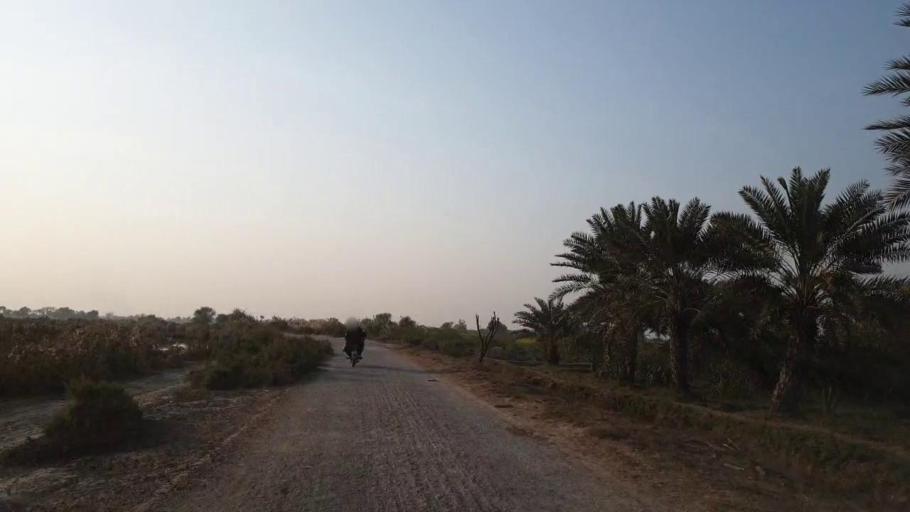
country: PK
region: Sindh
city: Pithoro
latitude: 25.6536
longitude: 69.2322
